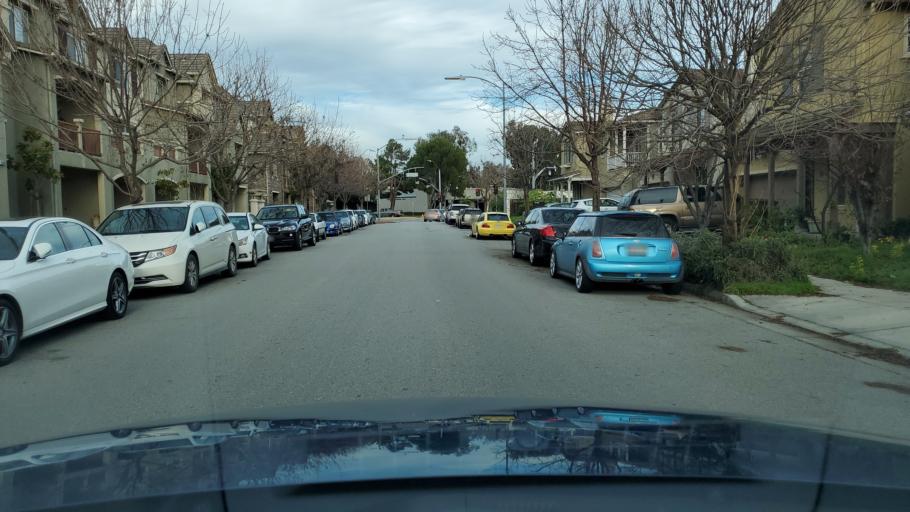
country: US
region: California
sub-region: Santa Clara County
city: Milpitas
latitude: 37.3932
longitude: -121.9027
